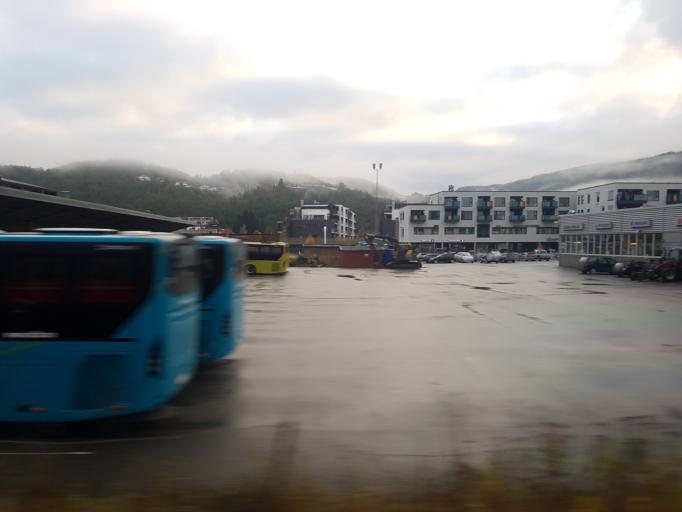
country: NO
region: Sor-Trondelag
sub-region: Melhus
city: Melhus
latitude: 63.2852
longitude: 10.2843
